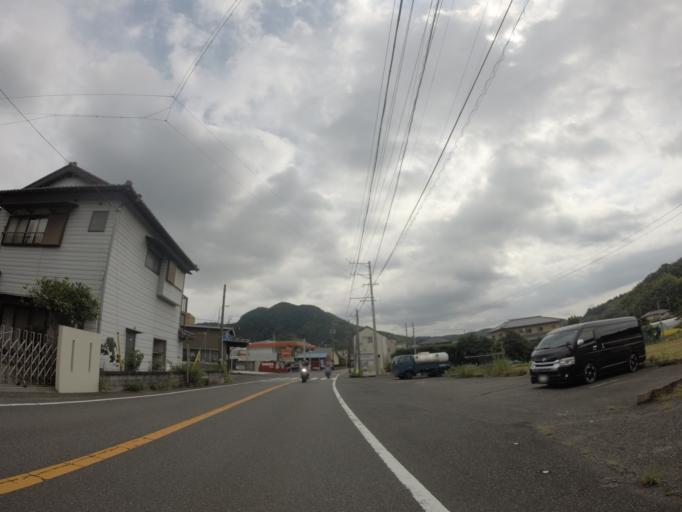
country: JP
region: Shizuoka
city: Fujieda
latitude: 34.8933
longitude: 138.2151
